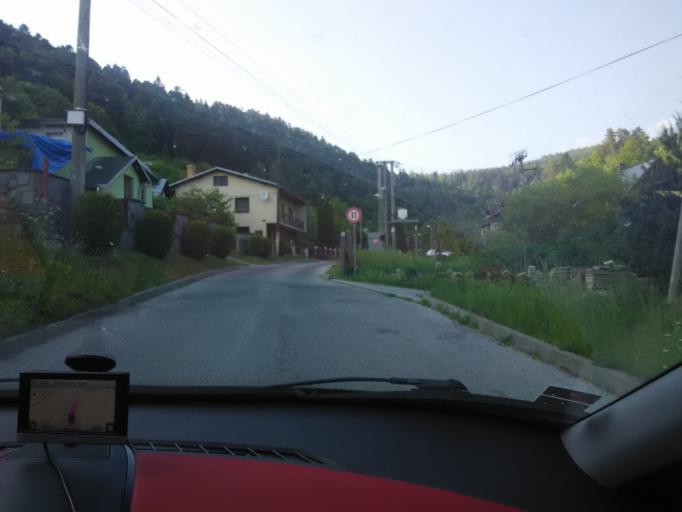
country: SK
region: Presovsky
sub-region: Okres Presov
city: Levoca
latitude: 49.0389
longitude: 20.6013
